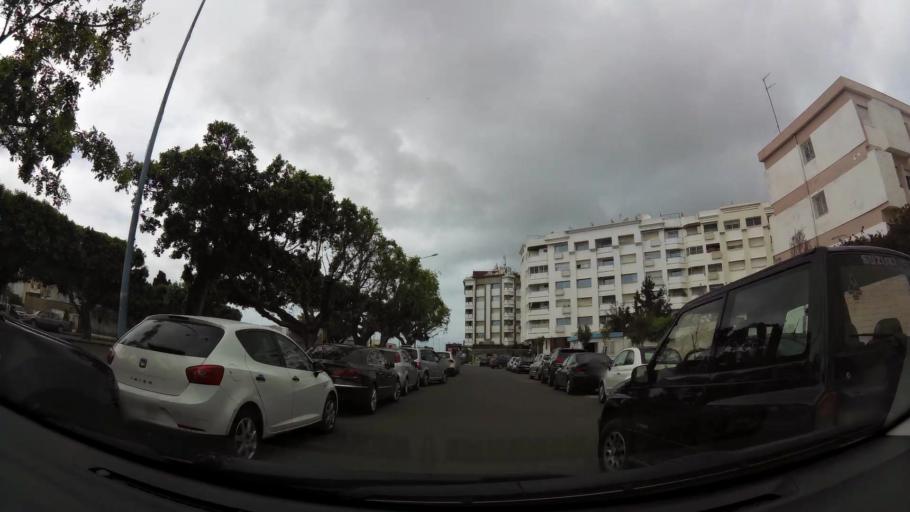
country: MA
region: Grand Casablanca
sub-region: Casablanca
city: Casablanca
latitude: 33.5946
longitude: -7.6452
